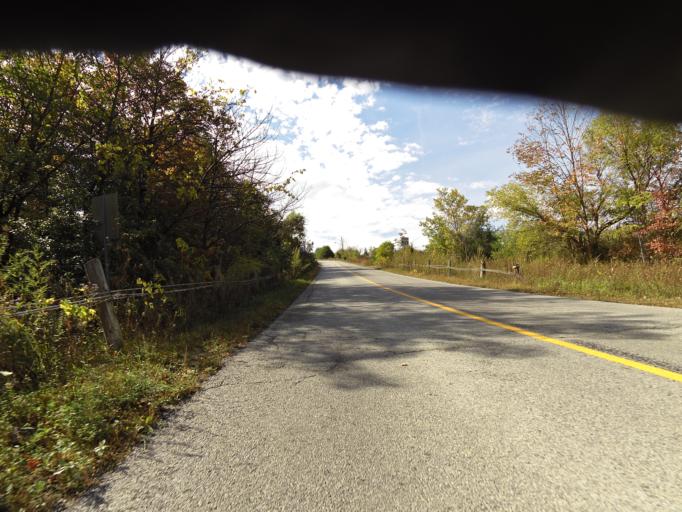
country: CA
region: Ontario
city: Hamilton
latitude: 43.3074
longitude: -79.8995
